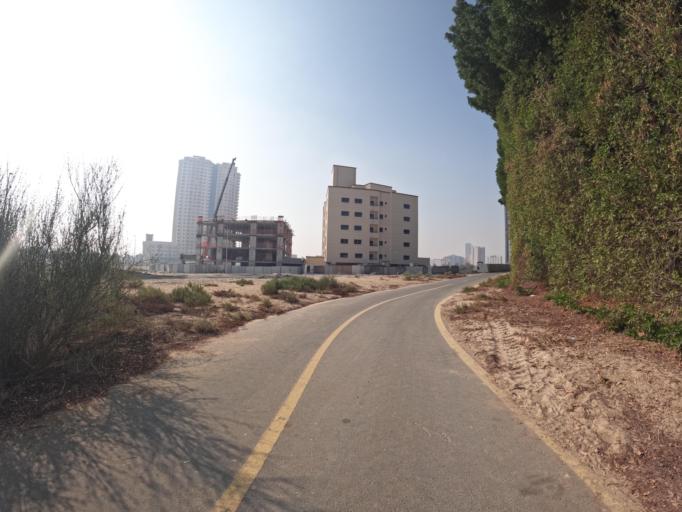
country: AE
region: Dubai
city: Dubai
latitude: 25.0967
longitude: 55.3244
